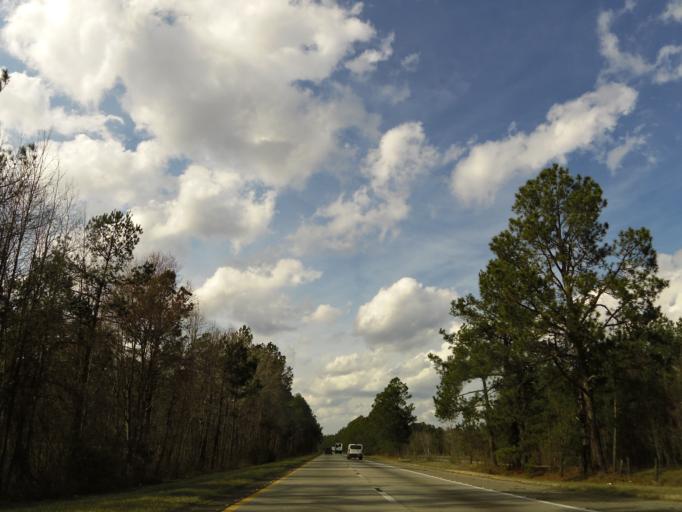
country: US
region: South Carolina
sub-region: Orangeburg County
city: Holly Hill
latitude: 33.2176
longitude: -80.4188
